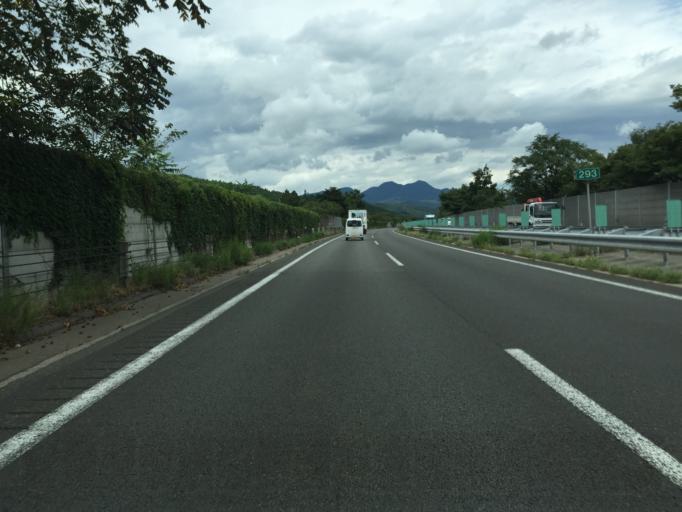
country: JP
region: Miyagi
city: Shiroishi
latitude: 37.9866
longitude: 140.6064
